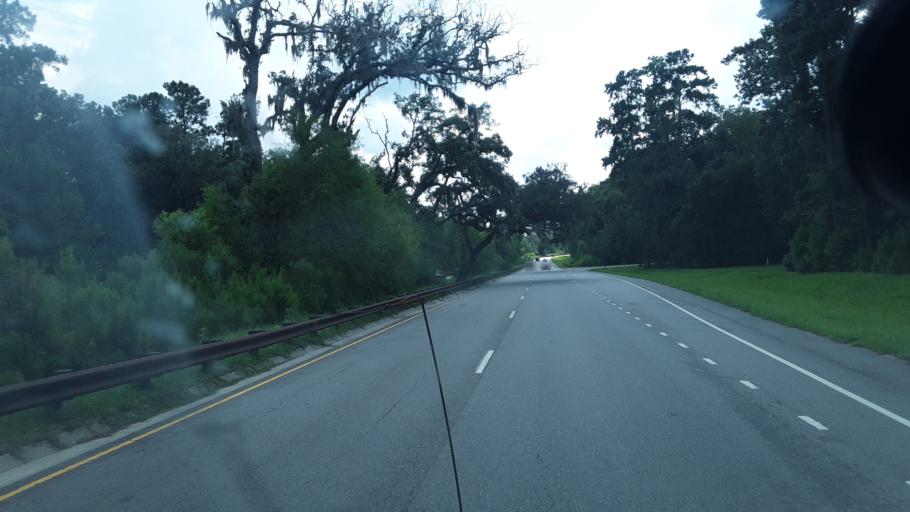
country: US
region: South Carolina
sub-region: Beaufort County
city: Bluffton
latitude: 32.2807
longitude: -80.9456
